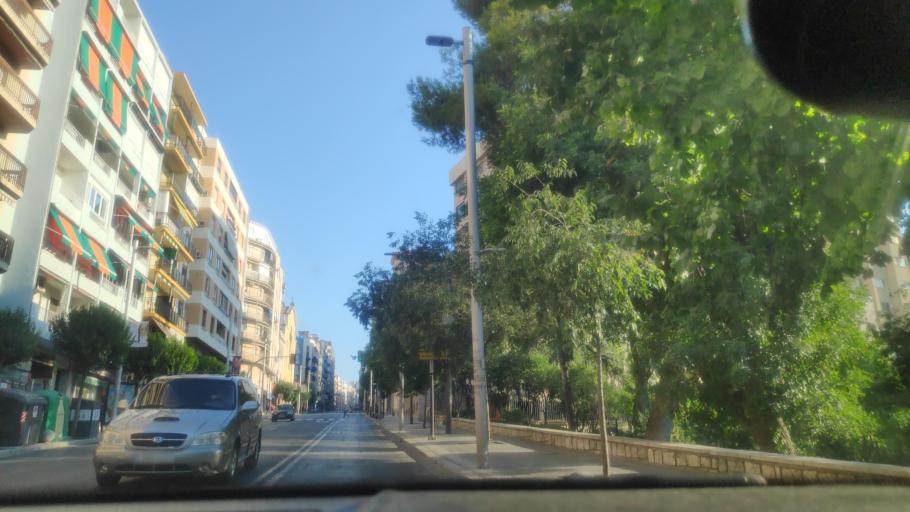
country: ES
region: Andalusia
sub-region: Provincia de Jaen
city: Jaen
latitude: 37.7726
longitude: -3.7862
